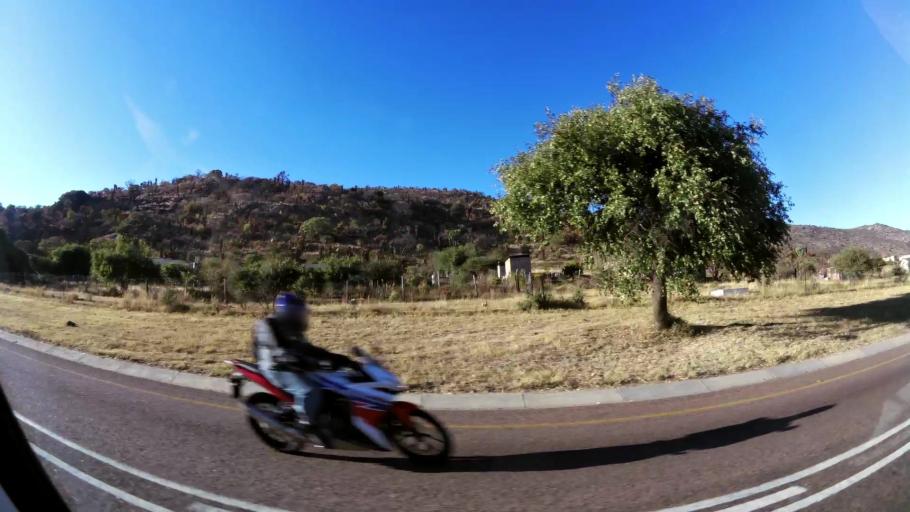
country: ZA
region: Limpopo
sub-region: Capricorn District Municipality
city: Mankoeng
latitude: -23.9378
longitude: 29.8304
